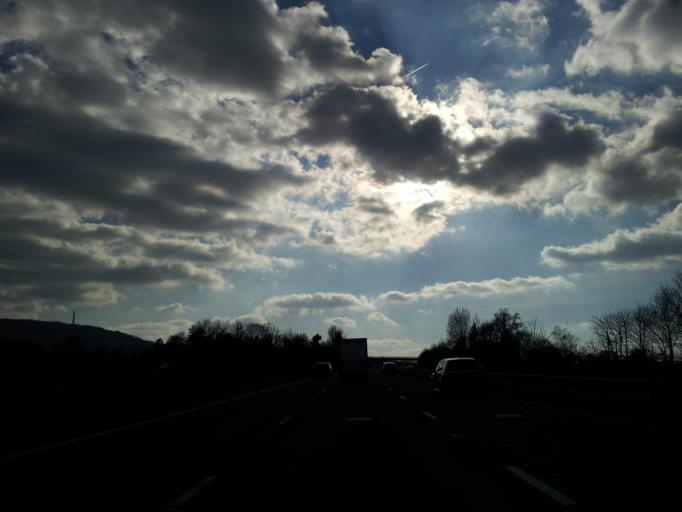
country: GB
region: England
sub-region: Somerset
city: Bishops Lydeard
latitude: 50.9649
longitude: -3.2133
